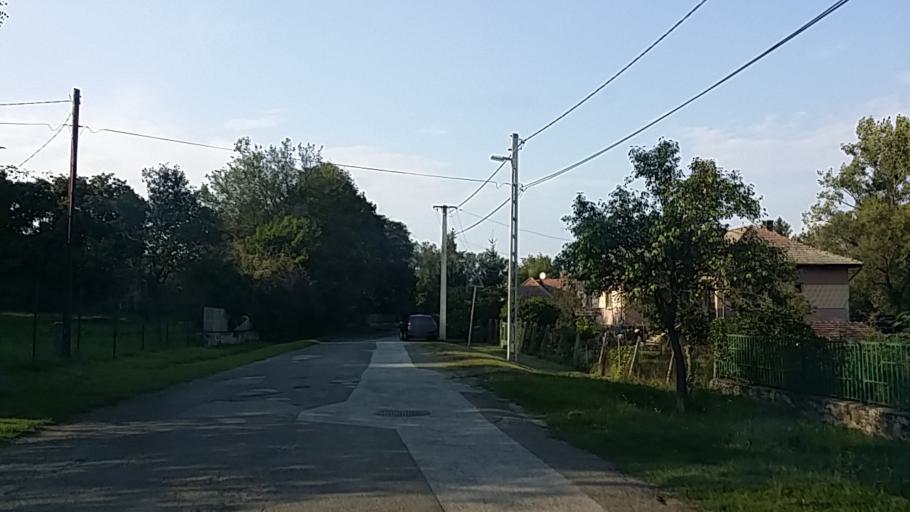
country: HU
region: Nograd
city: Bujak
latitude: 47.8253
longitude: 19.5343
